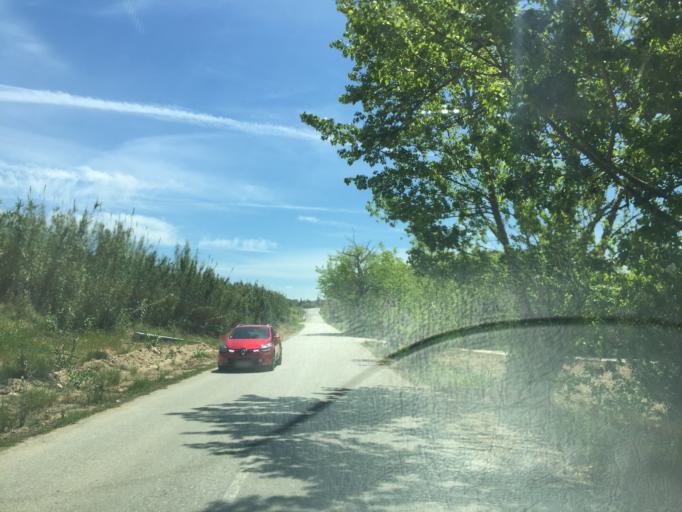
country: PT
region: Leiria
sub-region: Pombal
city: Lourical
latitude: 40.0692
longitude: -8.7316
